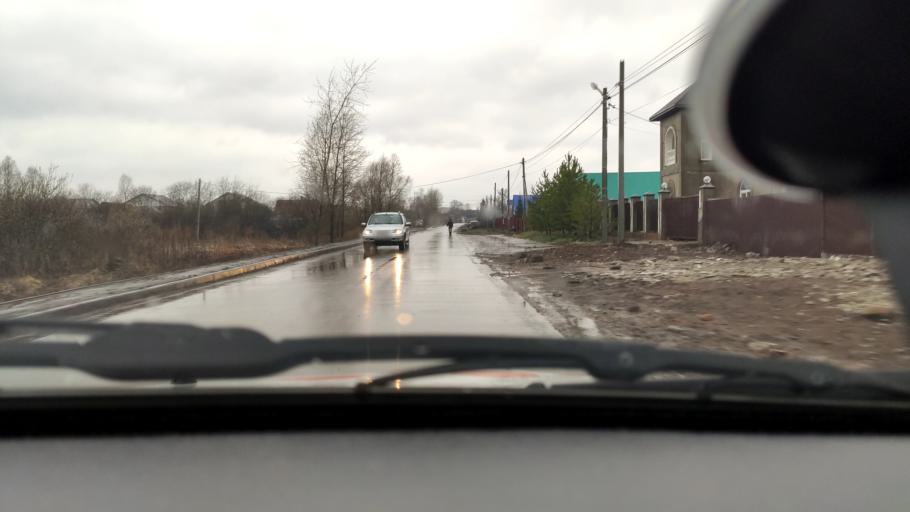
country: RU
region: Bashkortostan
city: Mikhaylovka
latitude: 54.7842
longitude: 55.8175
